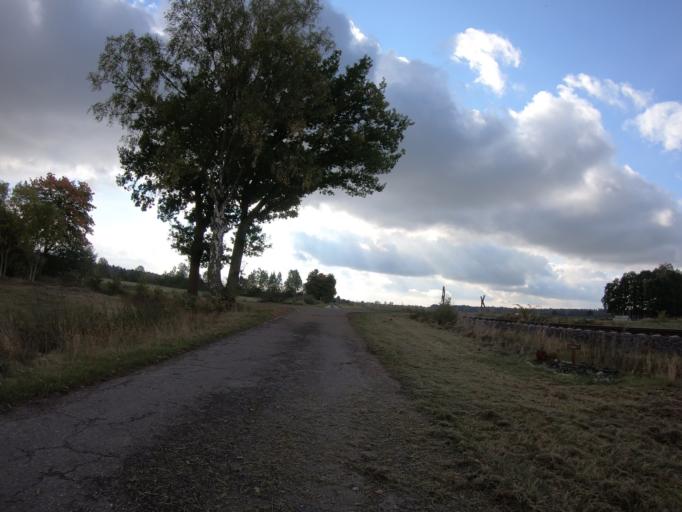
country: DE
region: Lower Saxony
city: Wahrenholz
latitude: 52.5869
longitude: 10.6096
